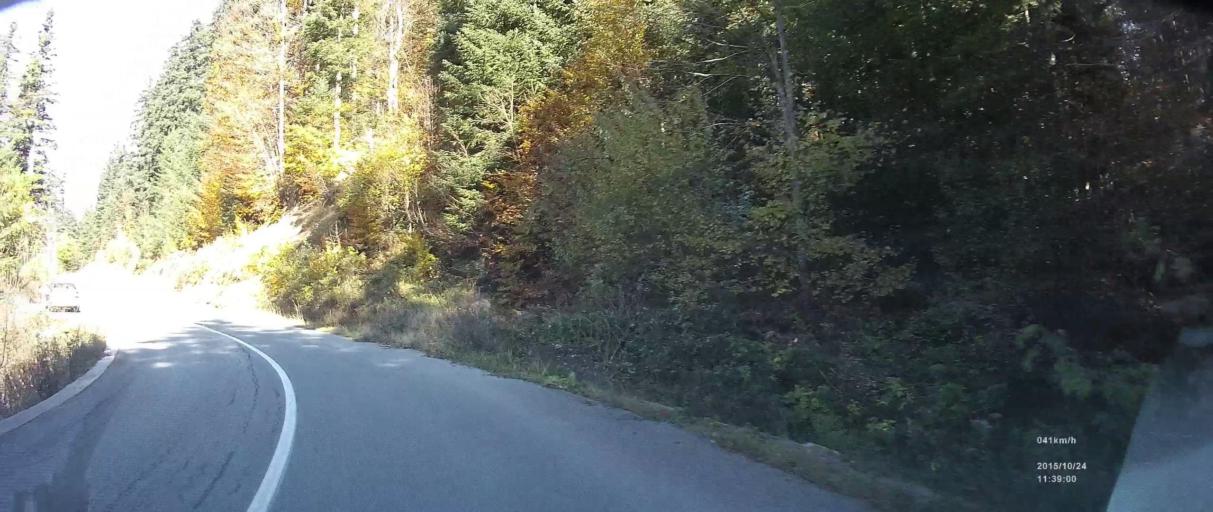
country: HR
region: Primorsko-Goranska
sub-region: Grad Delnice
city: Delnice
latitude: 45.4080
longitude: 14.7016
